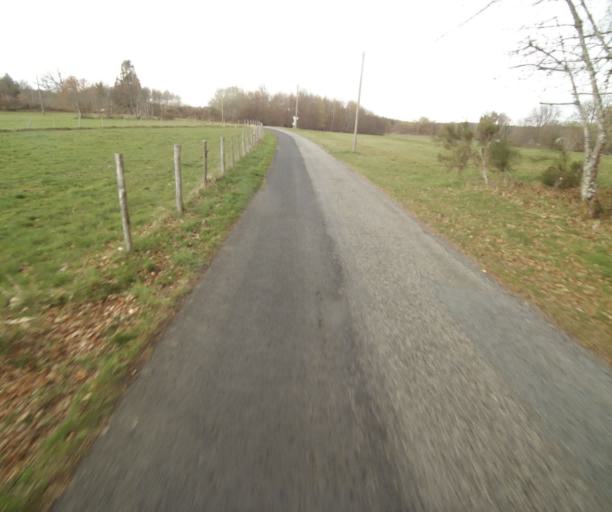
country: FR
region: Limousin
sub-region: Departement de la Correze
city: Egletons
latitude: 45.2597
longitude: 1.9924
